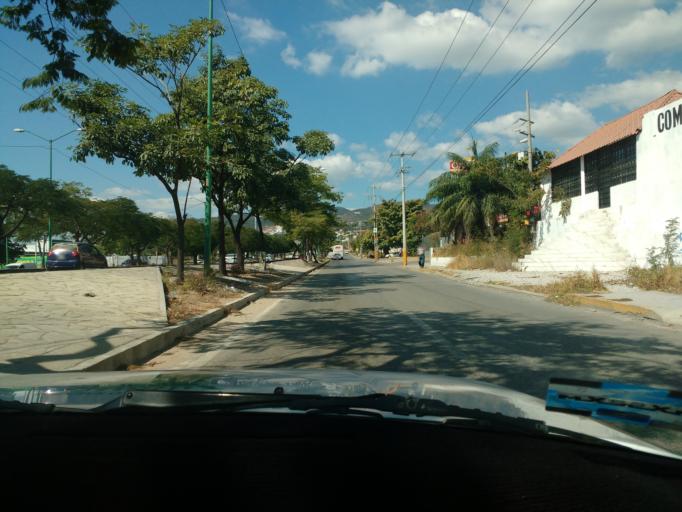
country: MX
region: Chiapas
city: Tuxtla Gutierrez
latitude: 16.7723
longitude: -93.1163
